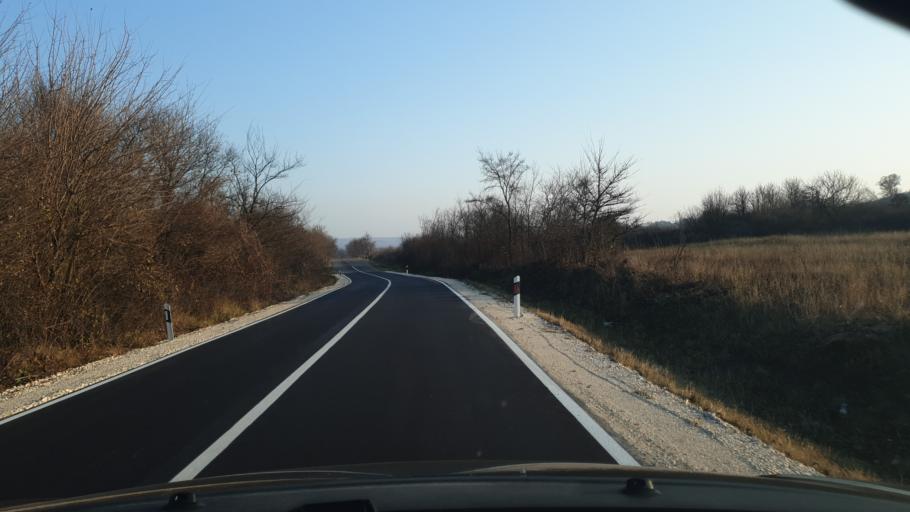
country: RS
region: Central Serbia
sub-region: Zajecarski Okrug
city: Zajecar
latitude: 43.9767
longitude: 22.2936
